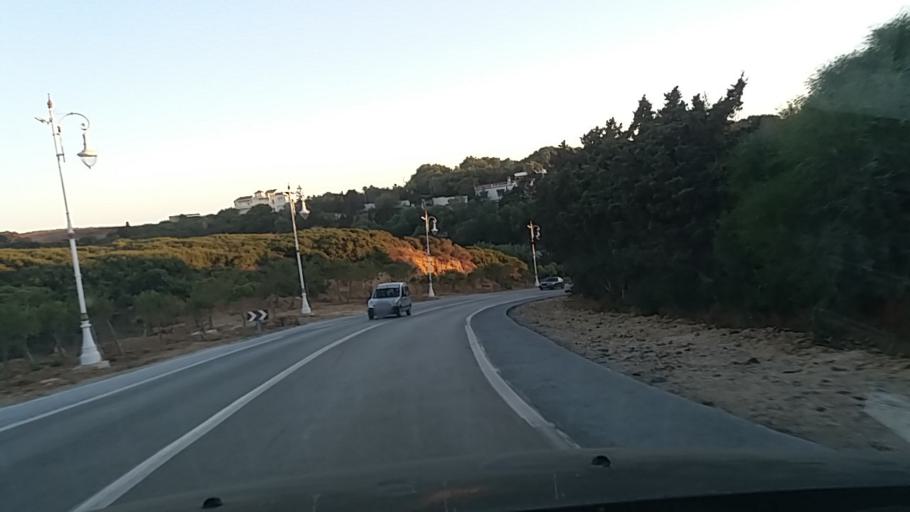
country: MA
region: Tanger-Tetouan
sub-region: Tanger-Assilah
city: Boukhalef
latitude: 35.7620
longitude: -5.9343
